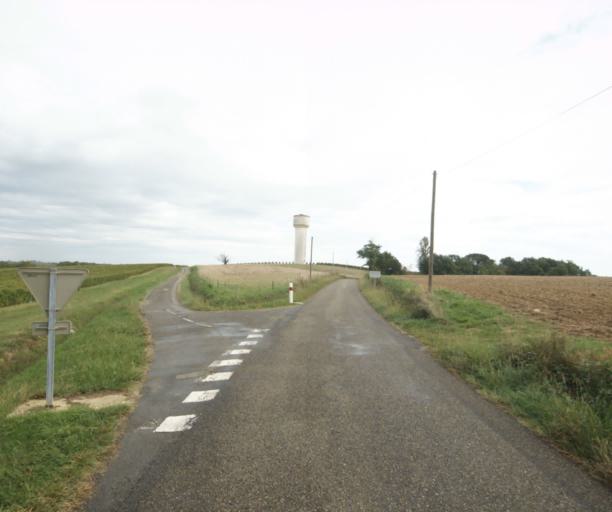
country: FR
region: Midi-Pyrenees
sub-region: Departement du Gers
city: Cazaubon
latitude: 43.8923
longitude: -0.1178
